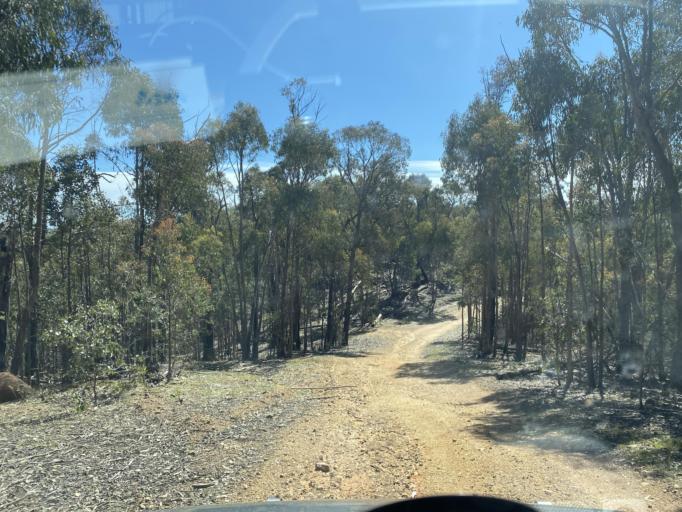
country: AU
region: Victoria
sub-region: Benalla
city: Benalla
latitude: -36.7235
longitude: 146.1813
